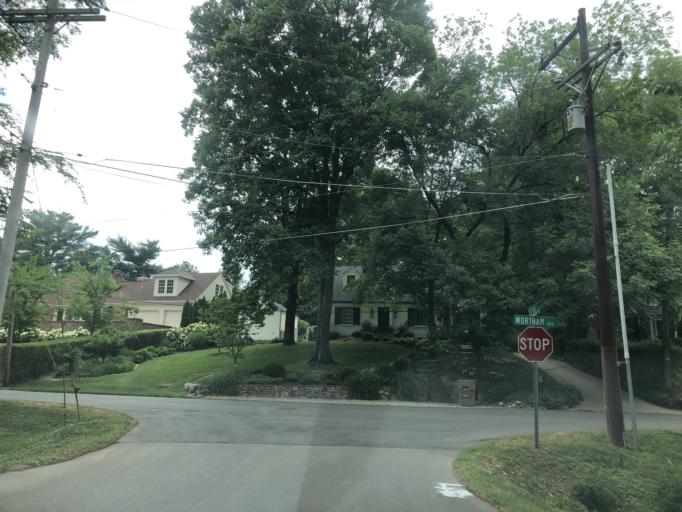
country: US
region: Tennessee
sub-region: Davidson County
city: Belle Meade
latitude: 36.1215
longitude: -86.8168
